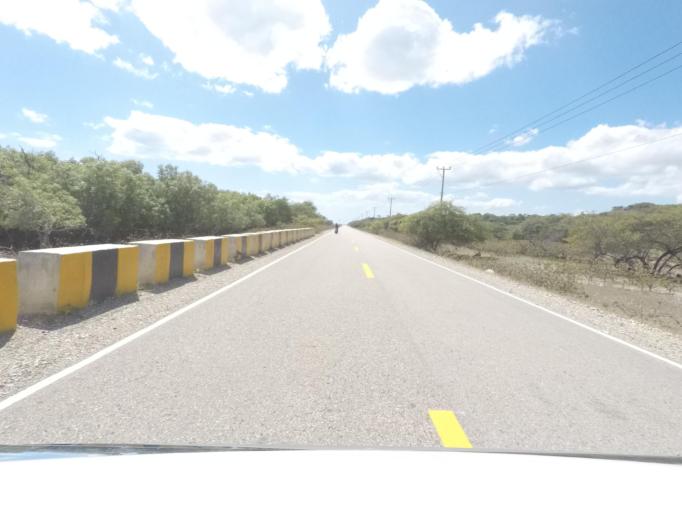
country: TL
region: Baucau
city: Baucau
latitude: -8.4407
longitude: 126.6559
